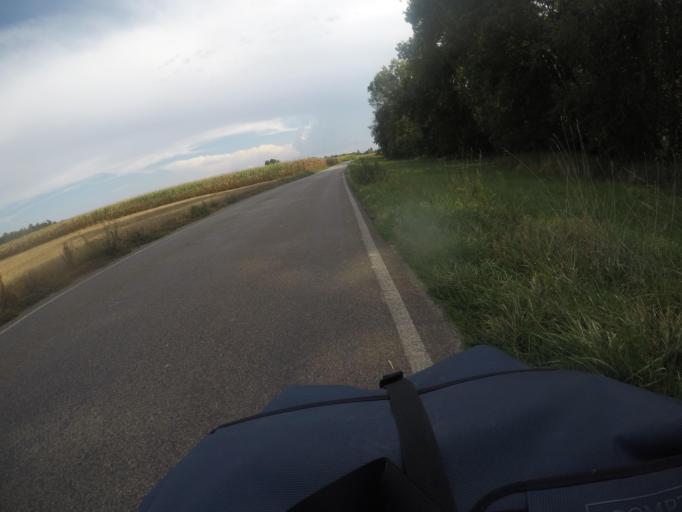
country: DE
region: Baden-Wuerttemberg
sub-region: Freiburg Region
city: Efringen-Kirchen
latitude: 47.6390
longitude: 7.5703
